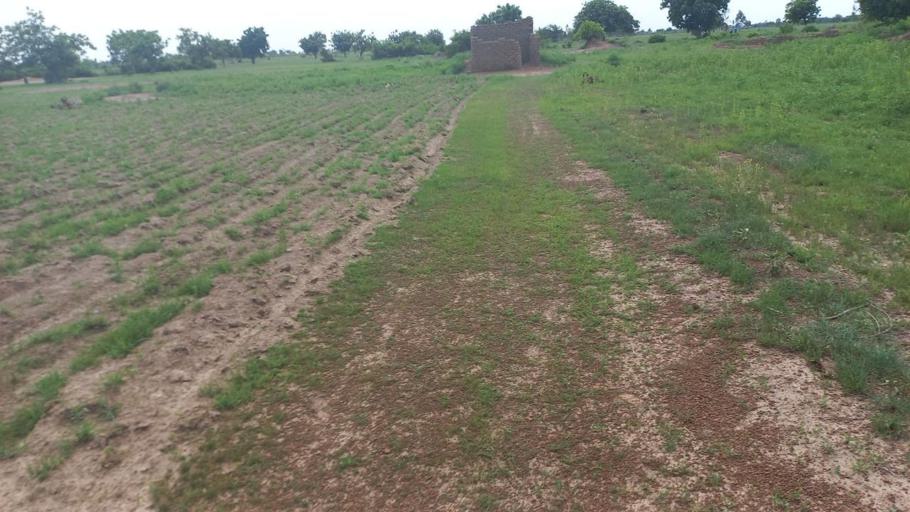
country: ML
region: Koulikoro
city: Dioila
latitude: 12.7638
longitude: -6.9244
